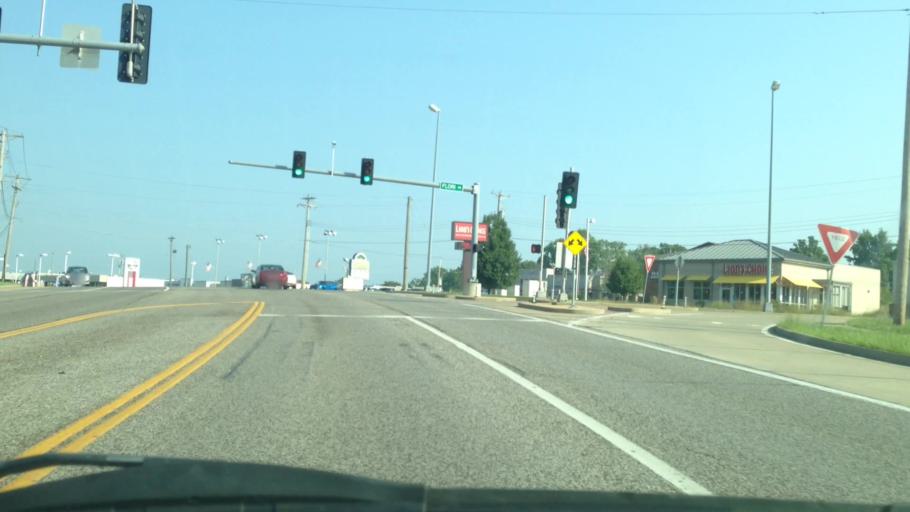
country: US
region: Missouri
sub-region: Saint Louis County
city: Green Park
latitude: 38.5191
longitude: -90.3430
